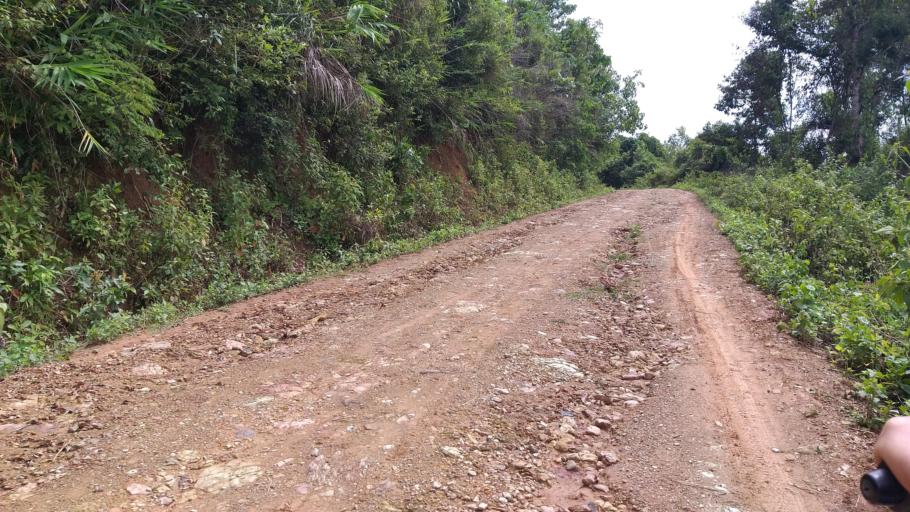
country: LA
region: Phongsali
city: Khoa
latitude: 21.3939
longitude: 102.6480
